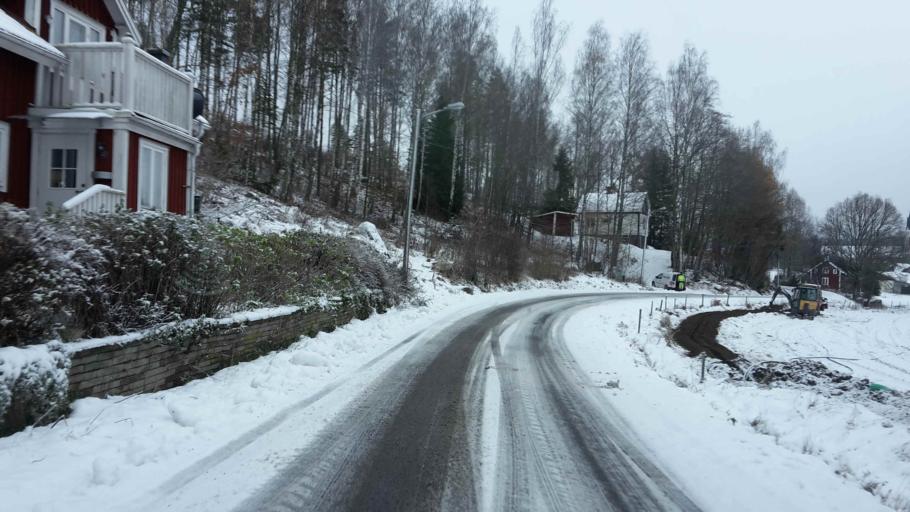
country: SE
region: Kalmar
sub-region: Vasterviks Kommun
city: Overum
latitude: 58.1560
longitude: 16.3304
